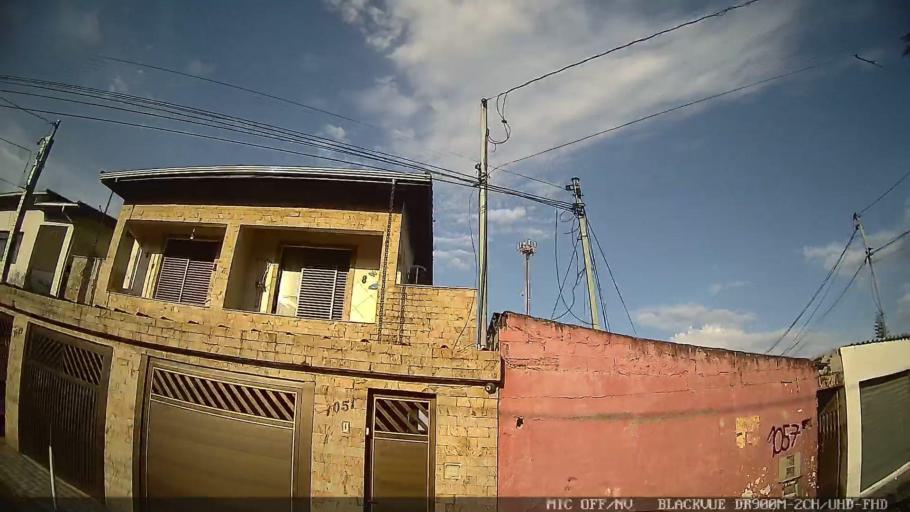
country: BR
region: Sao Paulo
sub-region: Cubatao
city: Cubatao
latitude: -23.9002
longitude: -46.4254
